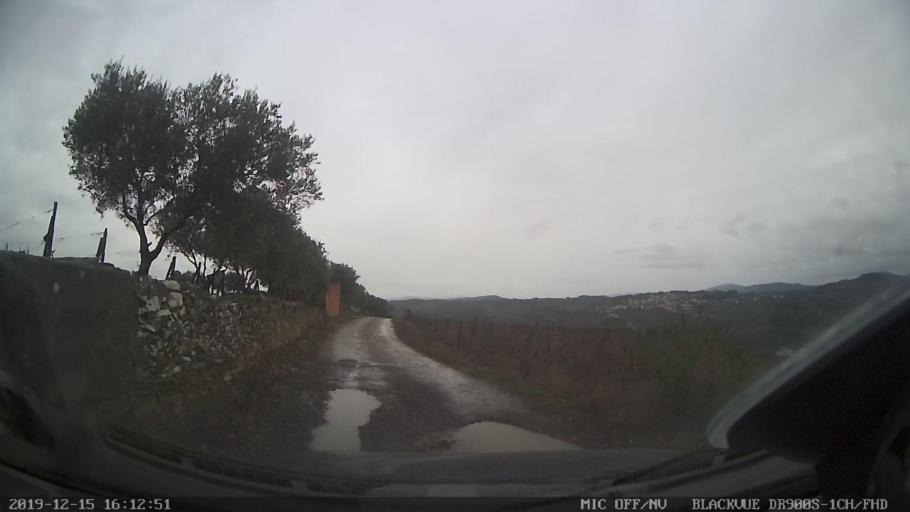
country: PT
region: Viseu
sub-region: Armamar
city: Armamar
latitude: 41.1748
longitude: -7.7129
